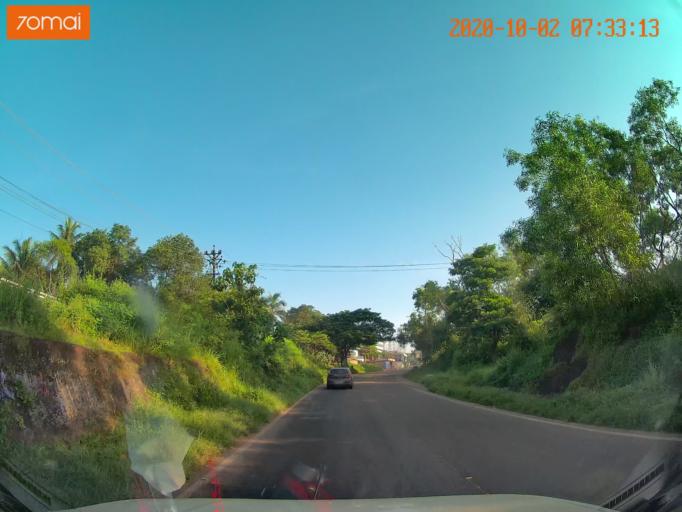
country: IN
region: Kerala
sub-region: Malappuram
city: Pariyapuram
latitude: 11.0572
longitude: 75.9354
